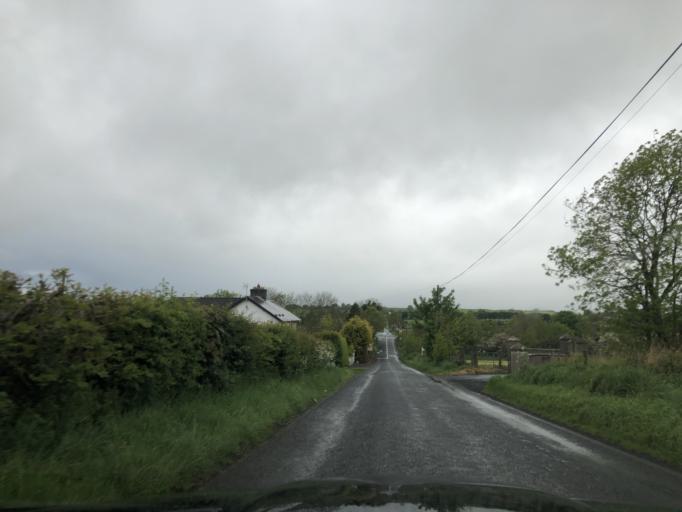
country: GB
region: Northern Ireland
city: Dunloy
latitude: 55.1216
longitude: -6.3600
